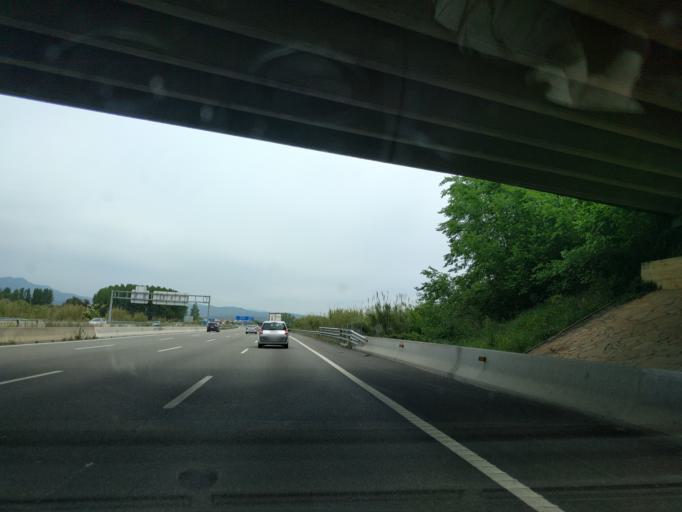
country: ES
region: Catalonia
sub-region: Provincia de Girona
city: Vilablareix
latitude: 41.9463
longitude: 2.7888
